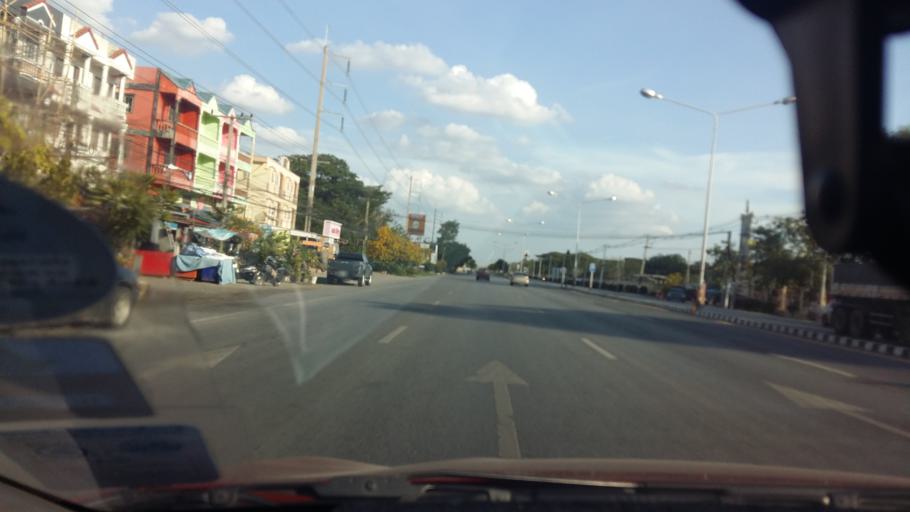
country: TH
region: Lop Buri
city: Lop Buri
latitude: 14.8415
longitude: 100.6439
